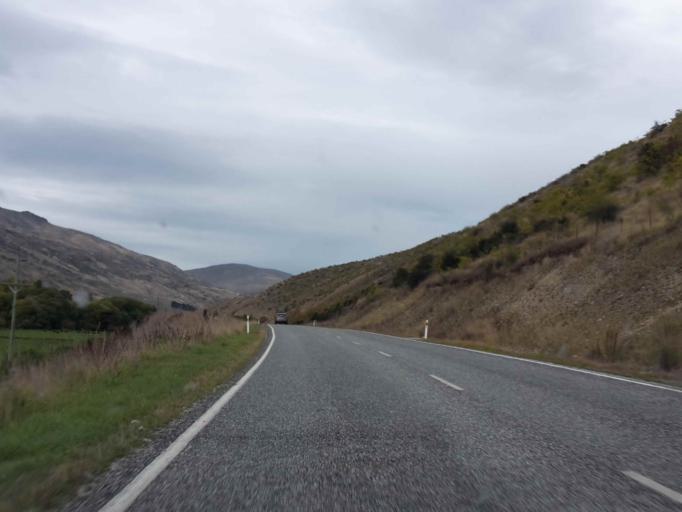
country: NZ
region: Otago
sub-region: Queenstown-Lakes District
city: Wanaka
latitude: -44.8109
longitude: 169.0664
